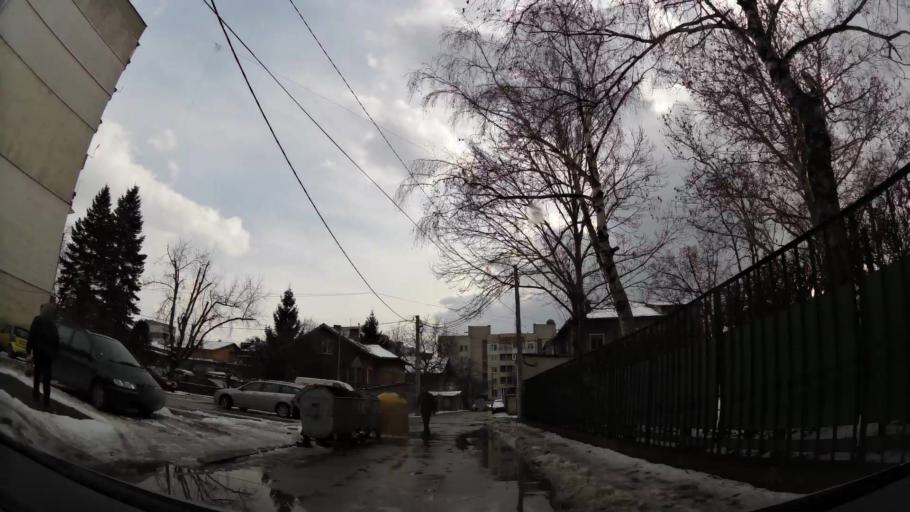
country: BG
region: Sofia-Capital
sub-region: Stolichna Obshtina
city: Sofia
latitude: 42.7034
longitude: 23.3692
